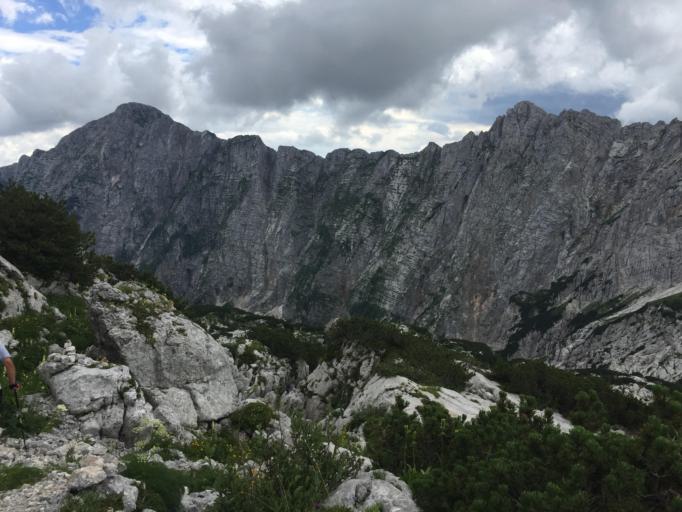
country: SI
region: Bovec
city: Bovec
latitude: 46.3881
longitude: 13.5272
